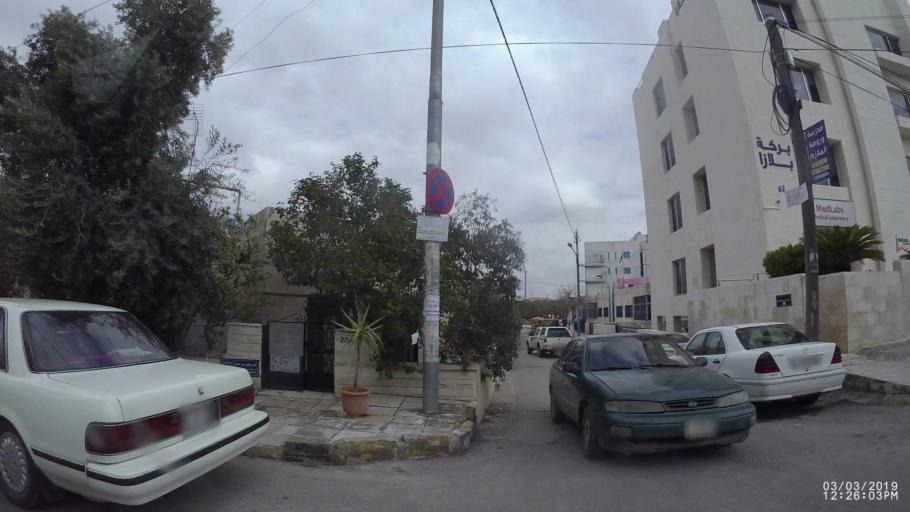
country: JO
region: Amman
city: Amman
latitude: 31.9788
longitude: 35.9014
